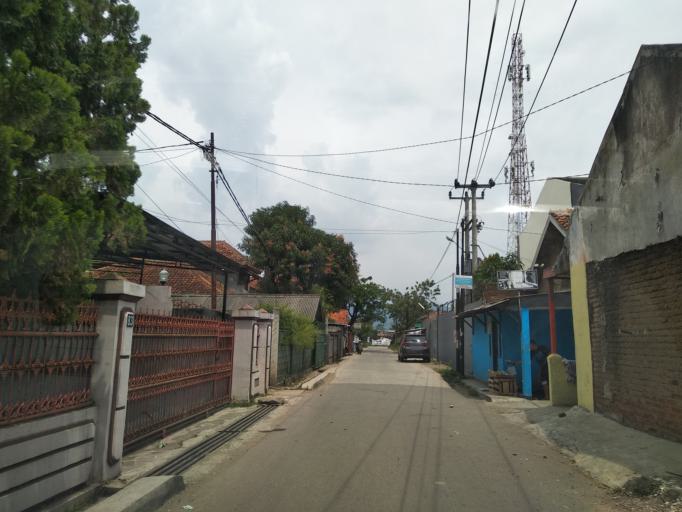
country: ID
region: West Java
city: Pameungpeuk
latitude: -6.9748
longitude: 107.6474
